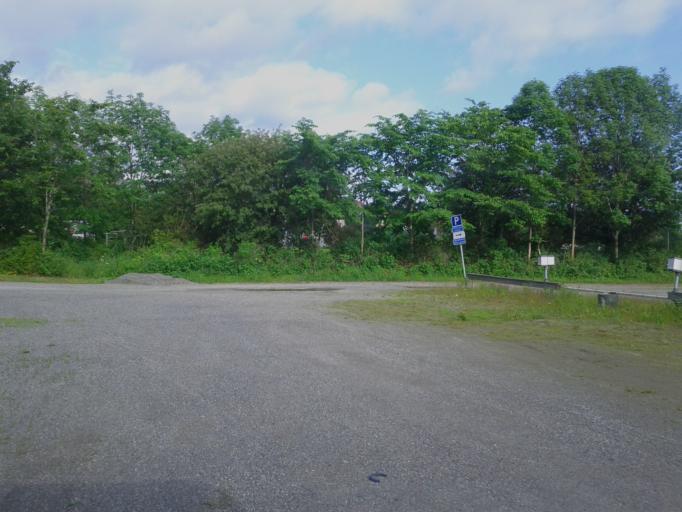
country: SE
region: Vaesternorrland
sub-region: OErnskoeldsviks Kommun
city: Ornskoldsvik
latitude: 63.2870
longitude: 18.7248
